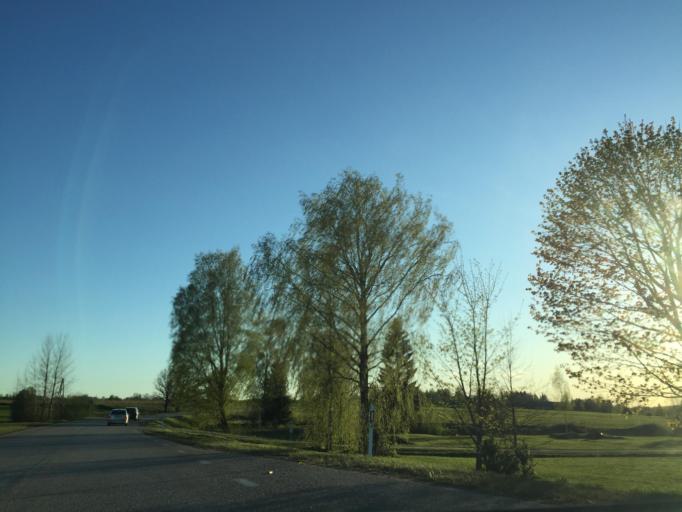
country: LV
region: Skriveri
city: Skriveri
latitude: 56.8834
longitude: 25.2648
